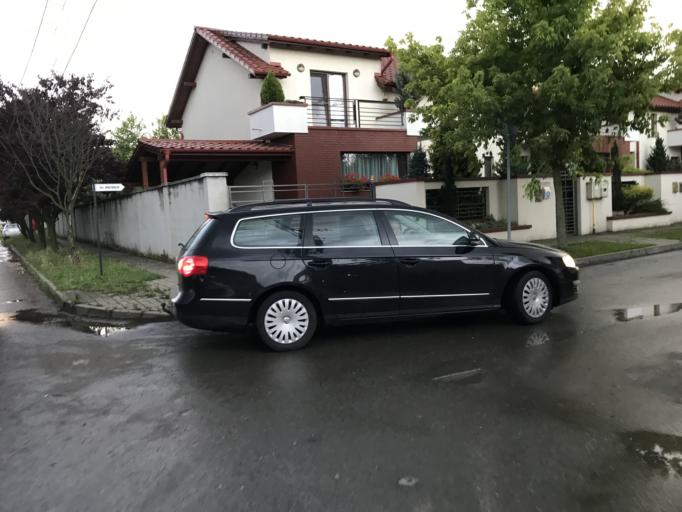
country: RO
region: Timis
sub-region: Comuna Dumbravita
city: Dumbravita
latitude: 45.7885
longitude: 21.2336
